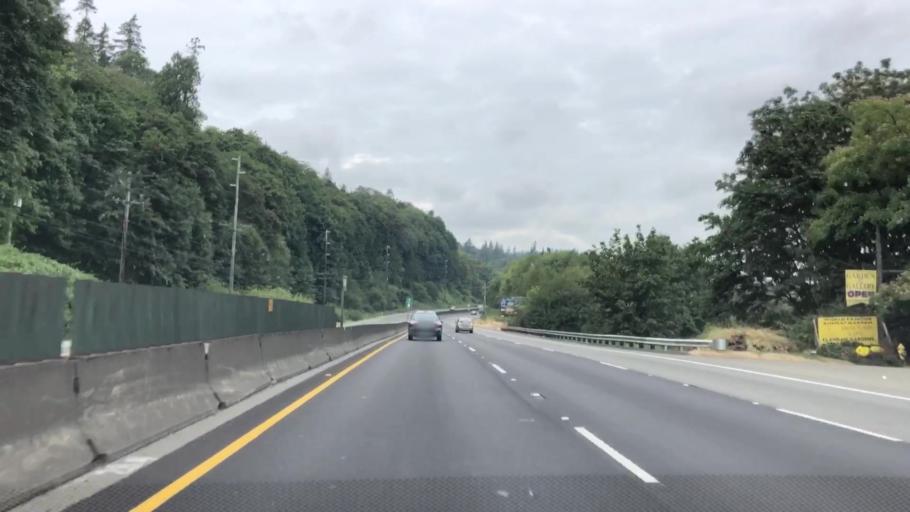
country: US
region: Washington
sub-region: Kitsap County
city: Navy Yard City
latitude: 47.5262
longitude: -122.6880
